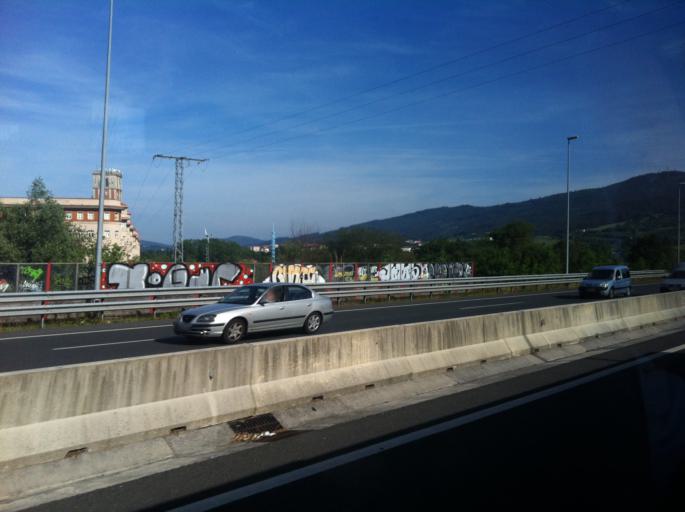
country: ES
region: Basque Country
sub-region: Bizkaia
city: Derio
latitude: 43.2943
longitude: -2.8819
